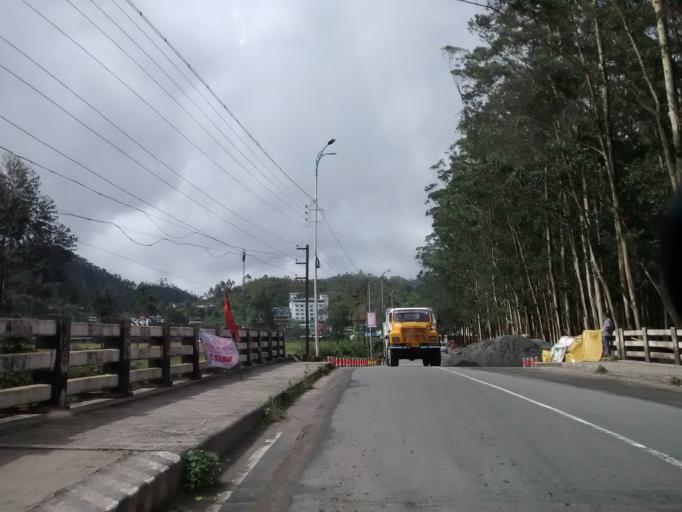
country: IN
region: Kerala
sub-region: Idukki
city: Munnar
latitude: 10.0702
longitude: 77.0608
